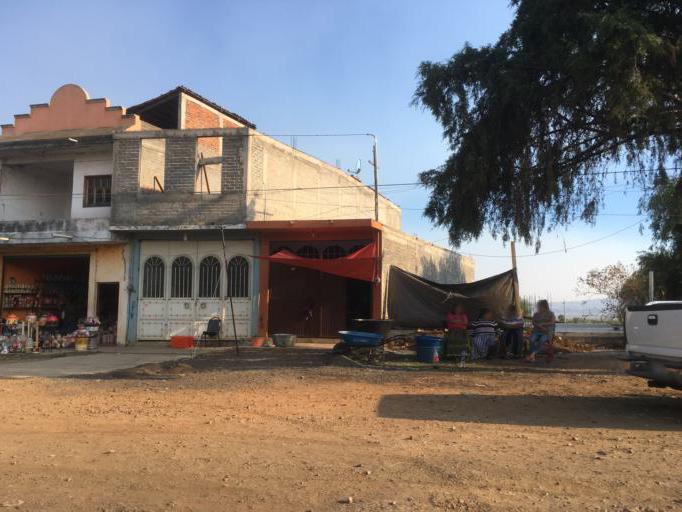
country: MX
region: Michoacan
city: Santa Fe de la Laguna
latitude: 19.6713
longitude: -101.5566
